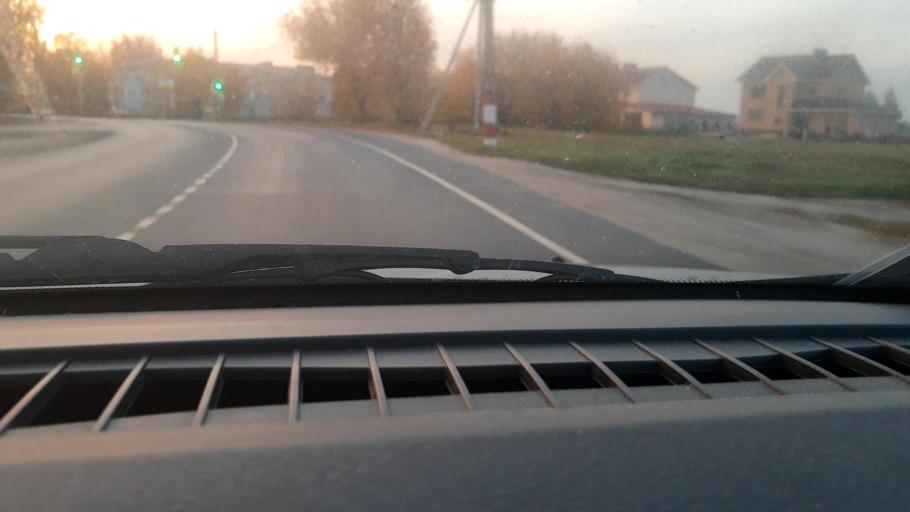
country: RU
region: Nizjnij Novgorod
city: Nizhniy Novgorod
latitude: 56.3774
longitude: 44.0213
